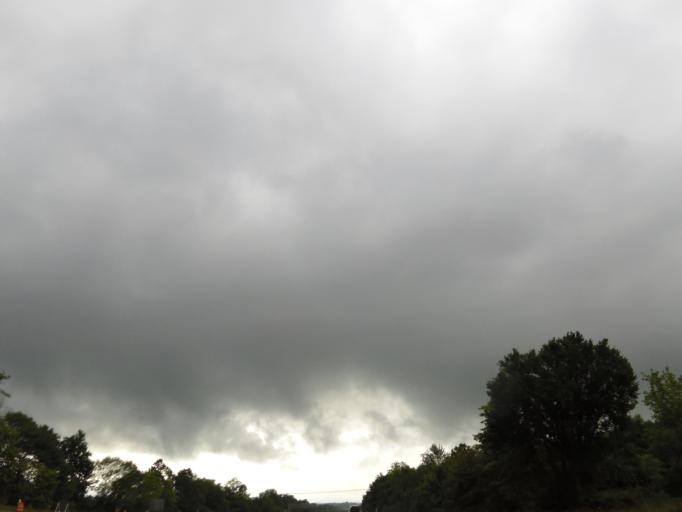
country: US
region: Illinois
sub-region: Jefferson County
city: Mount Vernon
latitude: 38.3398
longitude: -88.9628
